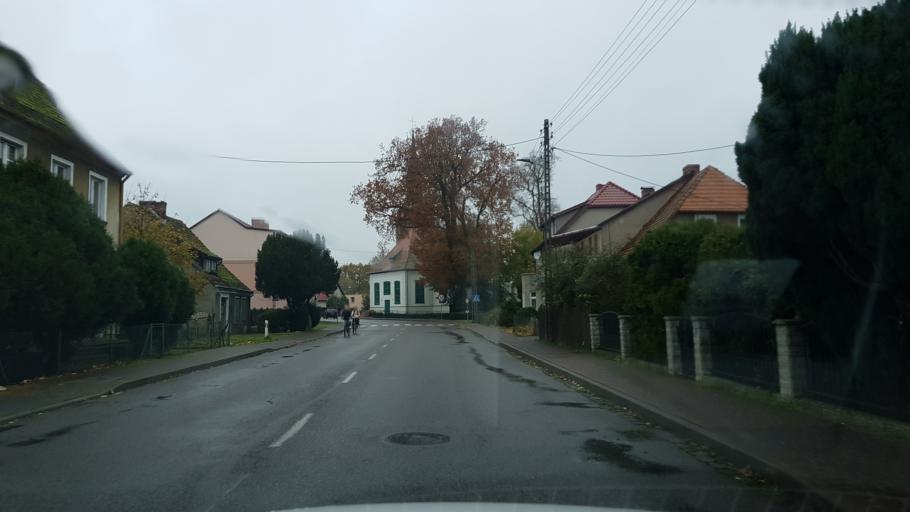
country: PL
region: West Pomeranian Voivodeship
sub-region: Powiat goleniowski
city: Stepnica
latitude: 53.6526
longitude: 14.6239
